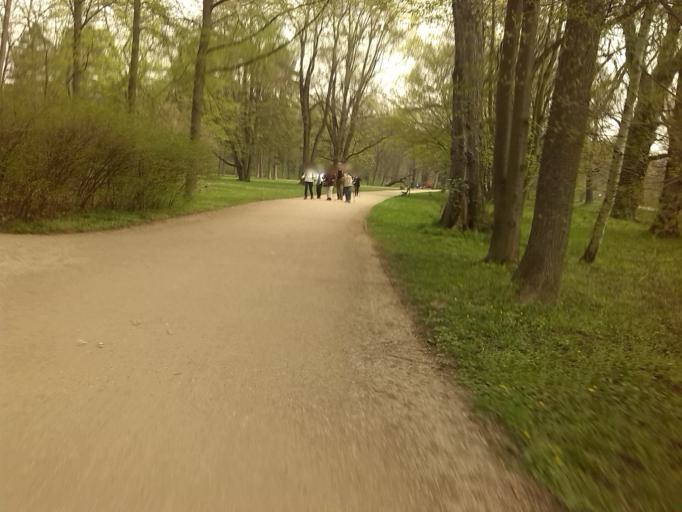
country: DE
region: Saxony
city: Dresden
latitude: 51.0359
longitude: 13.7683
